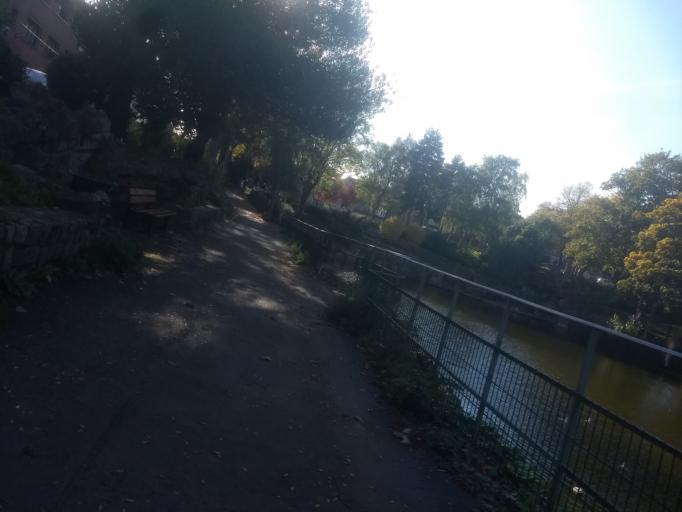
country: FR
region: Nord-Pas-de-Calais
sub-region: Departement du Pas-de-Calais
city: Arras
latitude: 50.2952
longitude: 2.7706
